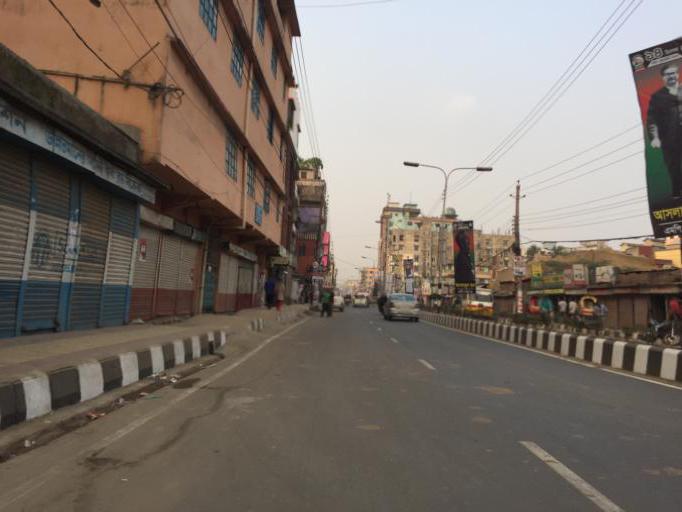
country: BD
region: Dhaka
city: Azimpur
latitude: 23.7847
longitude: 90.3474
